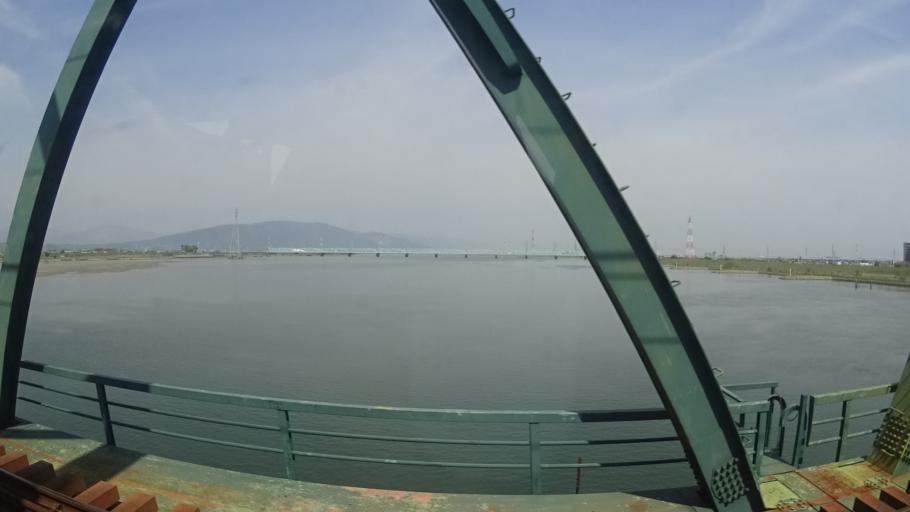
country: JP
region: Aichi
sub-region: Tsushima-shi
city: Tsushima
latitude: 35.1067
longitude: 136.7123
